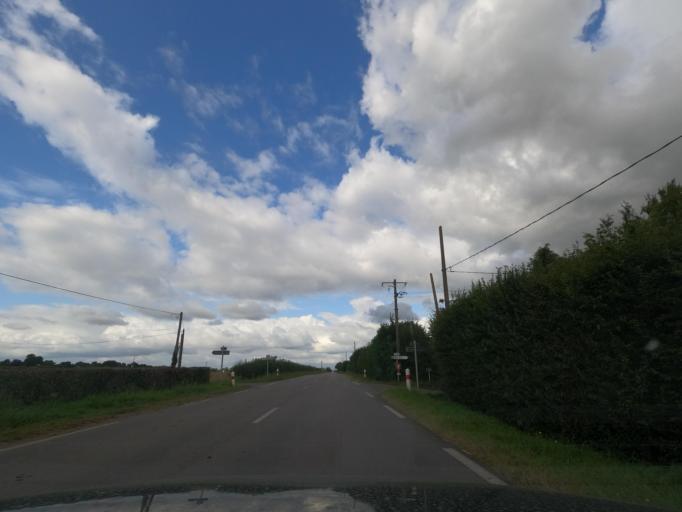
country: FR
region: Haute-Normandie
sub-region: Departement de l'Eure
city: Broglie
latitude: 48.9629
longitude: 0.4738
